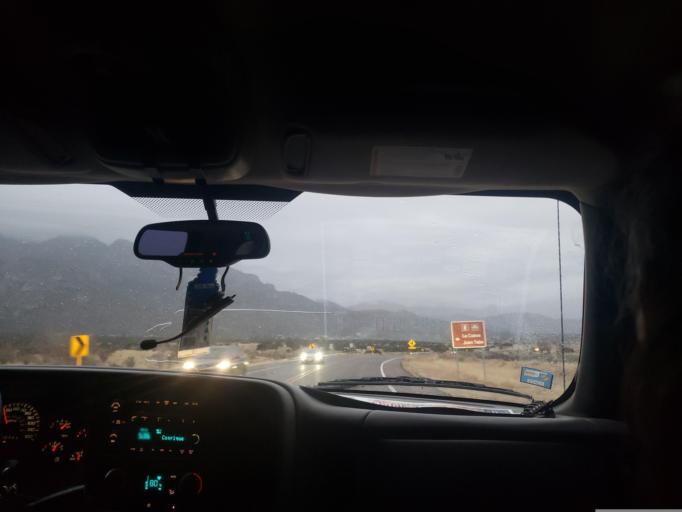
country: US
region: New Mexico
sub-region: Bernalillo County
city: Sandia Heights
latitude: 35.2012
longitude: -106.5084
